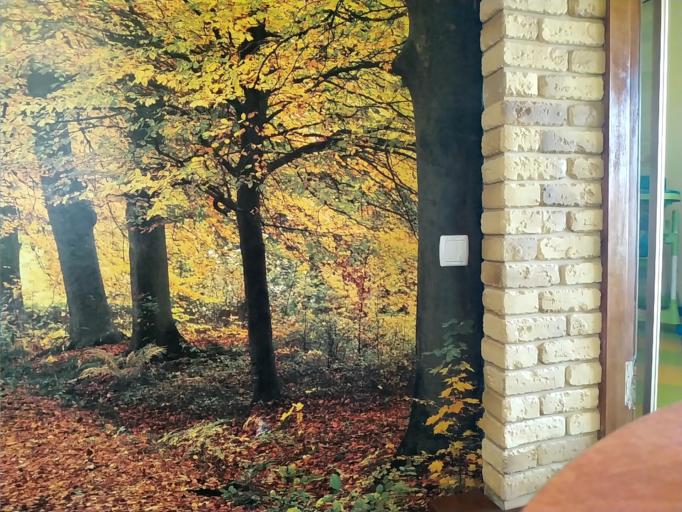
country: RU
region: Tverskaya
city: Maksatikha
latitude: 57.6108
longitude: 35.9124
